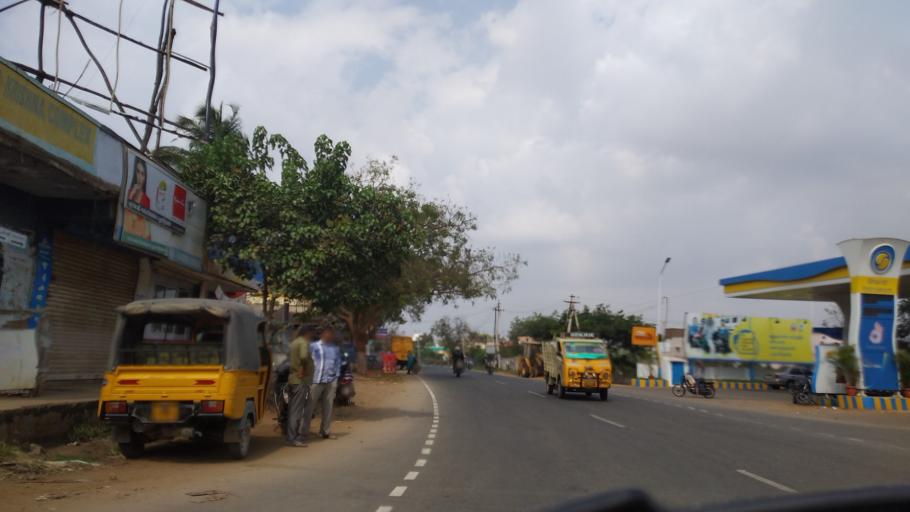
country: IN
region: Tamil Nadu
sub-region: Coimbatore
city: Perur
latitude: 10.9544
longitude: 76.9295
